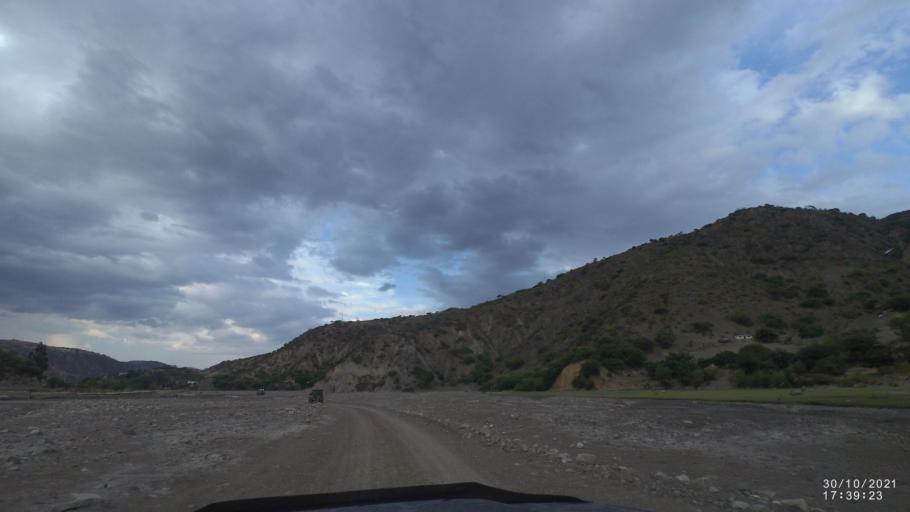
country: BO
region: Cochabamba
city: Sipe Sipe
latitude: -17.5311
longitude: -66.5544
